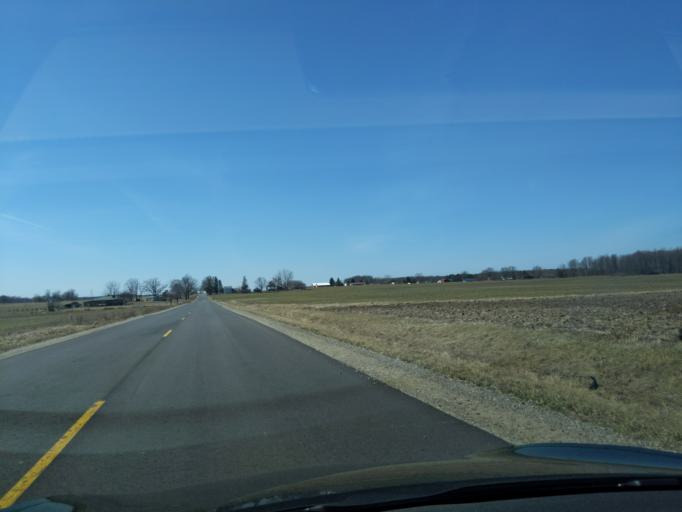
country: US
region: Michigan
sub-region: Eaton County
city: Grand Ledge
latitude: 42.7266
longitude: -84.8859
